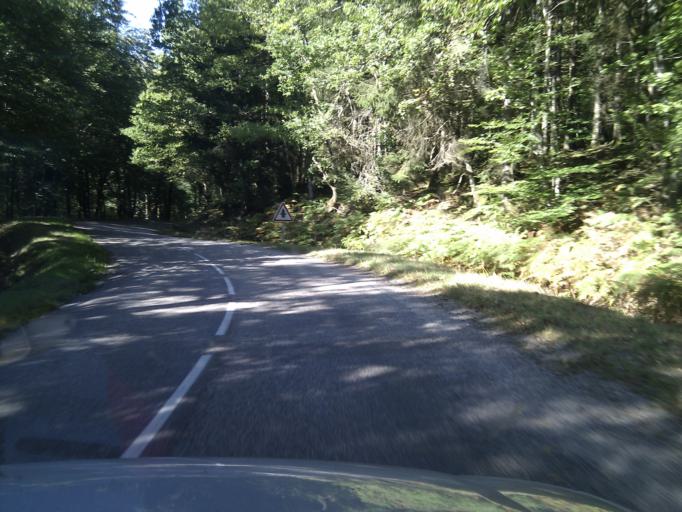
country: FR
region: Bourgogne
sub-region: Departement de la Cote-d'Or
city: Saulieu
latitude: 47.2471
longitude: 4.0493
